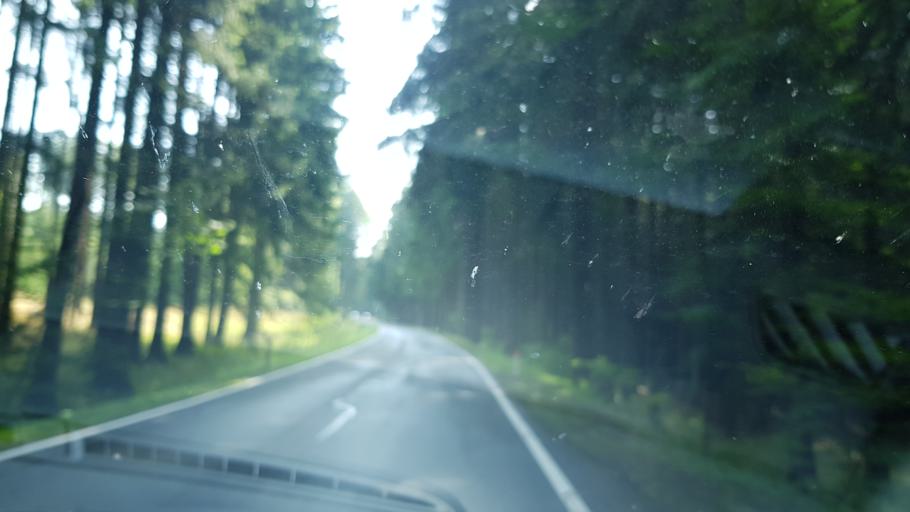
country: CZ
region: Olomoucky
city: Ceska Ves
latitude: 50.2186
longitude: 17.2666
